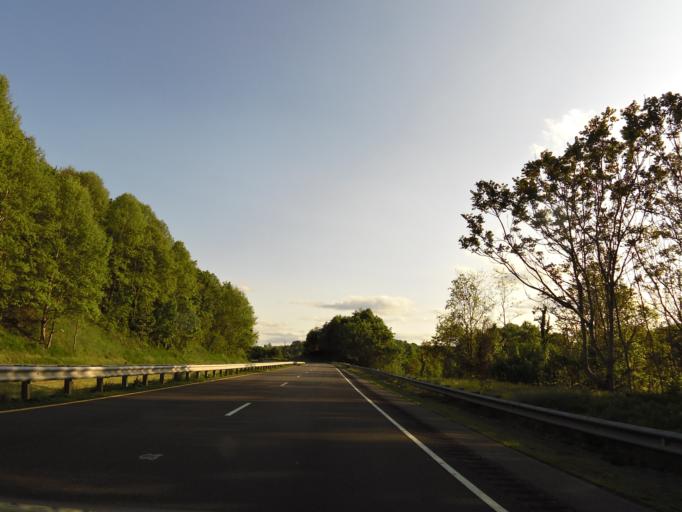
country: US
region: Virginia
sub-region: Russell County
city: Lebanon
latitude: 36.8723
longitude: -82.1111
